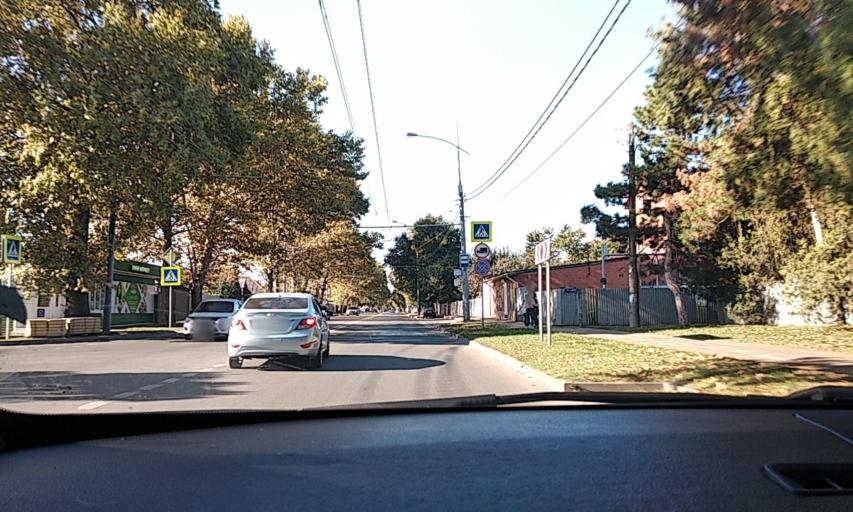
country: RU
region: Krasnodarskiy
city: Pashkovskiy
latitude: 45.0268
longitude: 39.1177
